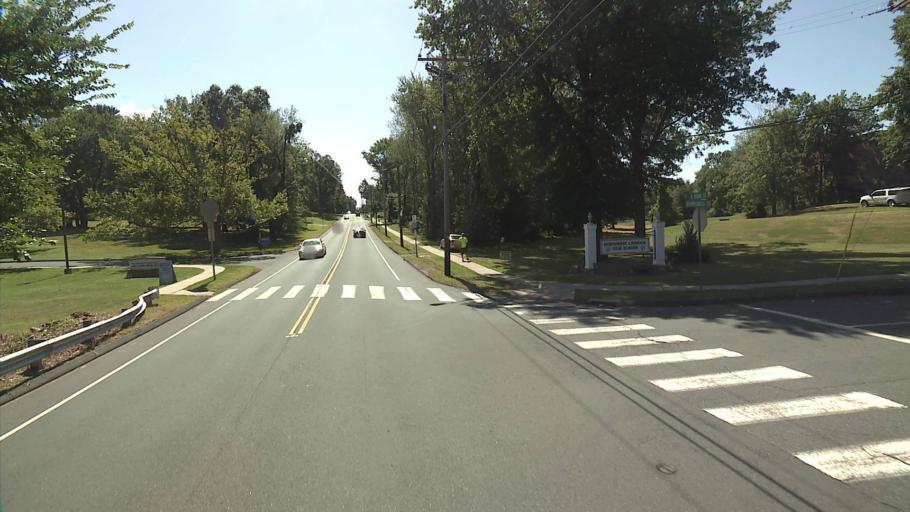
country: US
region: Connecticut
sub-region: Hartford County
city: West Hartford
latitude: 41.8007
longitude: -72.7498
